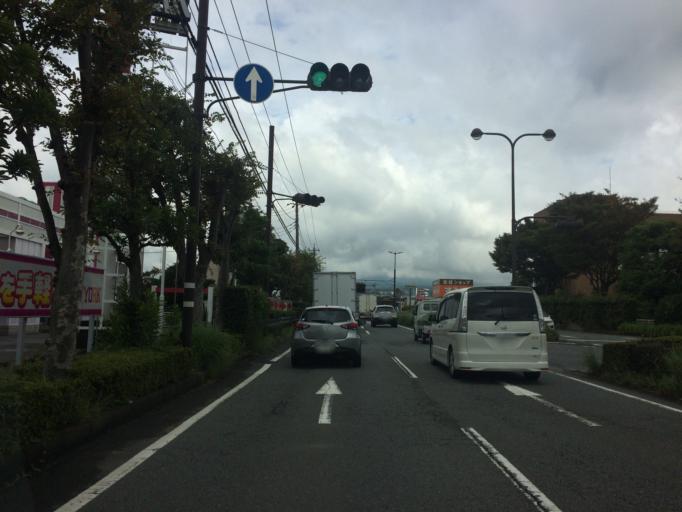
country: JP
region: Shizuoka
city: Fuji
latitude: 35.1641
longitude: 138.6694
